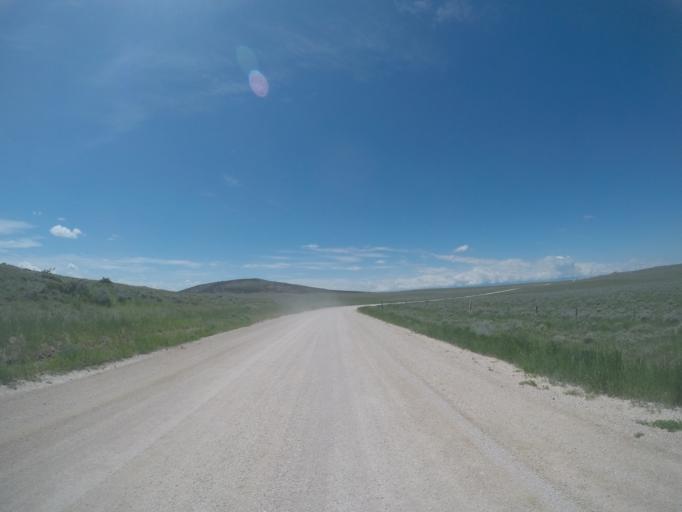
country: US
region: Wyoming
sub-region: Park County
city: Powell
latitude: 45.2057
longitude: -108.7312
